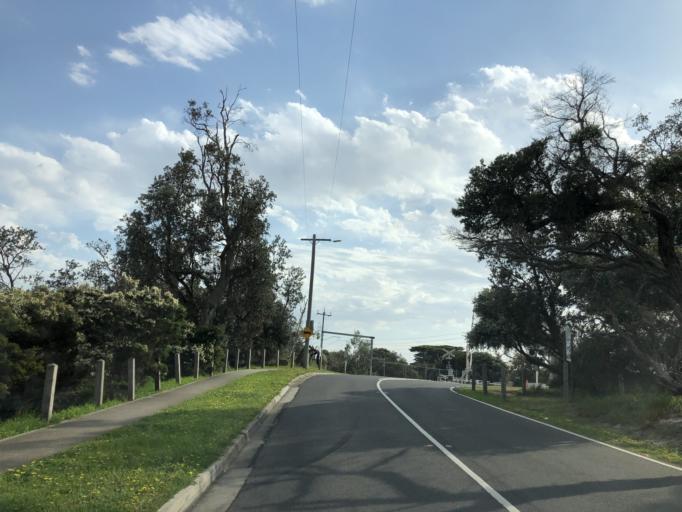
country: AU
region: Victoria
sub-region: Frankston
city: Seaford
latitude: -38.0936
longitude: 145.1277
